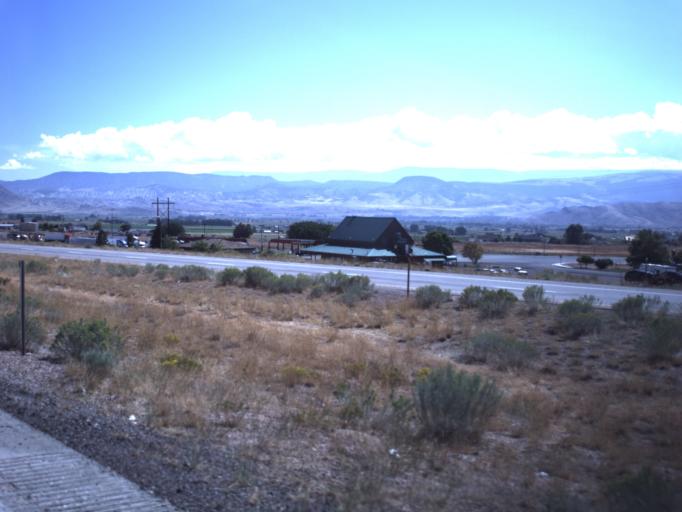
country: US
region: Utah
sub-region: Sevier County
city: Richfield
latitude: 38.7890
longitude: -112.0859
